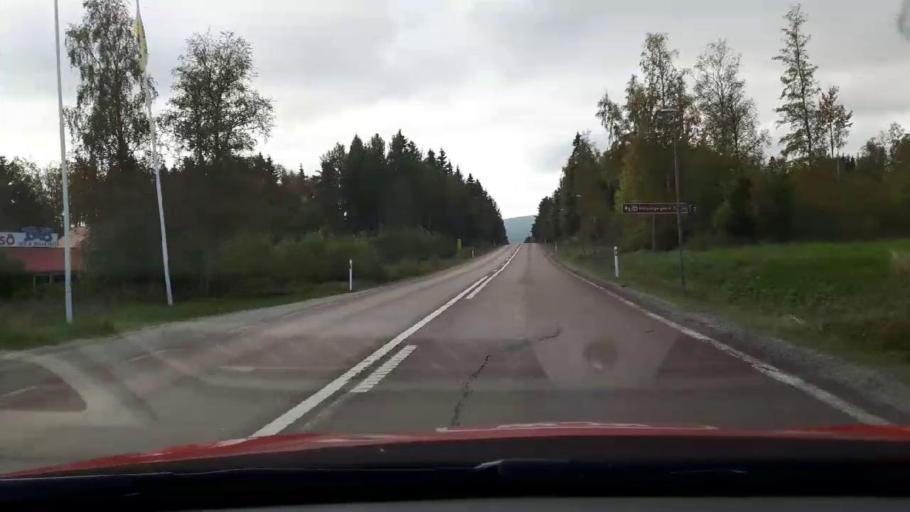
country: SE
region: Gaevleborg
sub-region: Ljusdals Kommun
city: Jaervsoe
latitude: 61.6878
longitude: 16.1487
